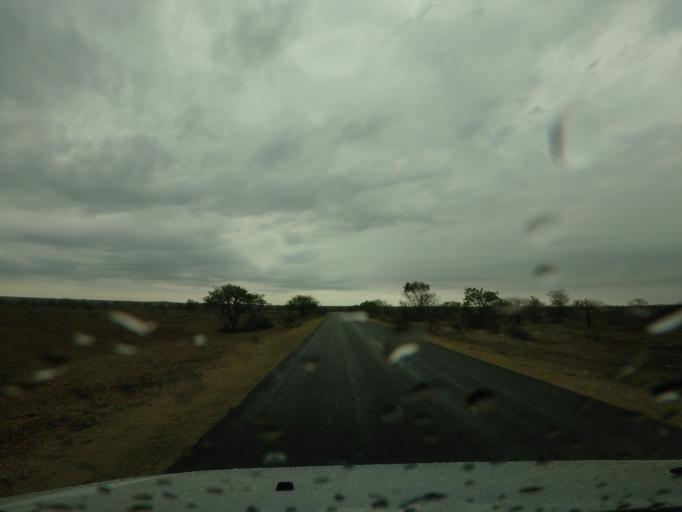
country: ZA
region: Limpopo
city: Thulamahashi
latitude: -24.4742
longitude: 31.4032
